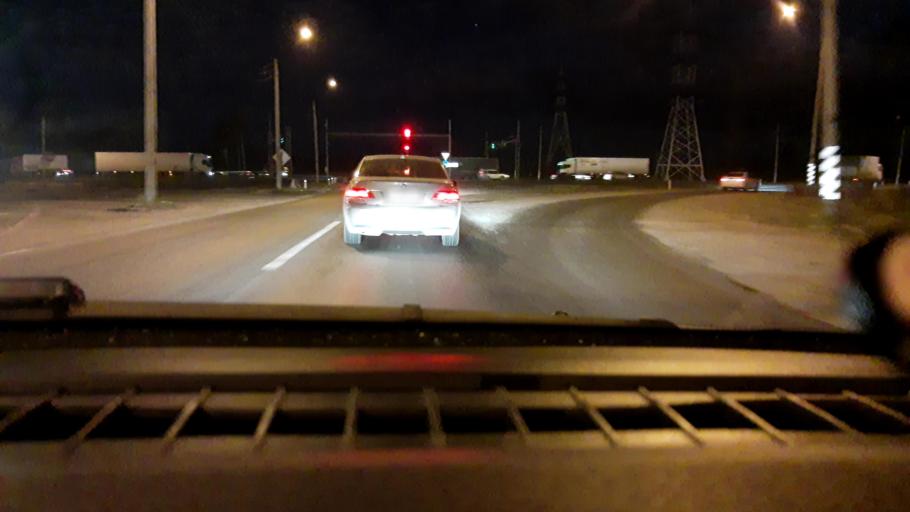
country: RU
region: Nizjnij Novgorod
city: Babino
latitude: 56.3031
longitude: 43.5594
